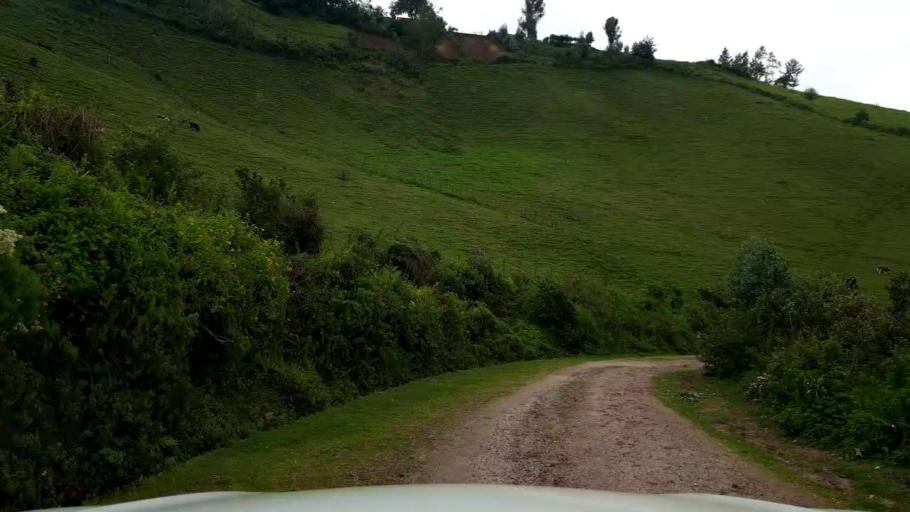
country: RW
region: Western Province
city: Gisenyi
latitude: -1.6759
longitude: 29.4170
